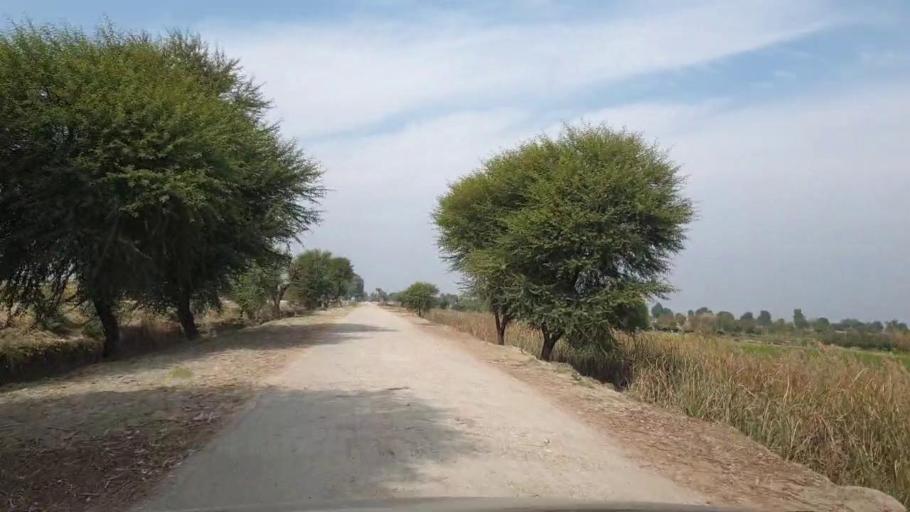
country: PK
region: Sindh
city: Khadro
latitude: 26.1199
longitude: 68.8027
